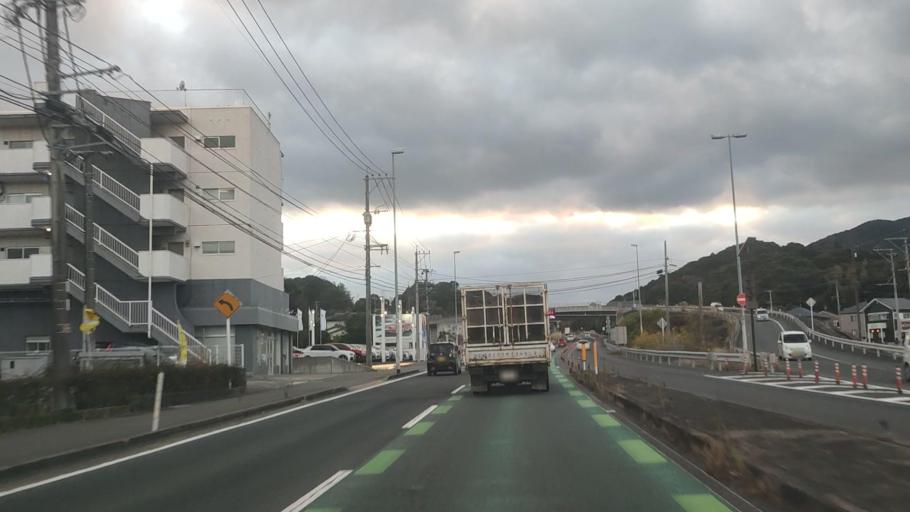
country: JP
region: Nagasaki
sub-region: Isahaya-shi
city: Isahaya
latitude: 32.8179
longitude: 129.9680
